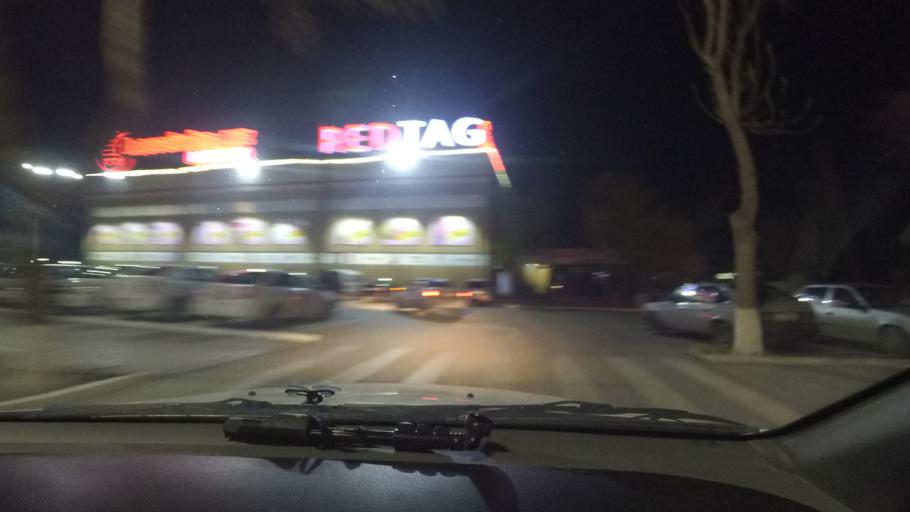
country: UZ
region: Bukhara
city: Bukhara
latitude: 39.7720
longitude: 64.4410
